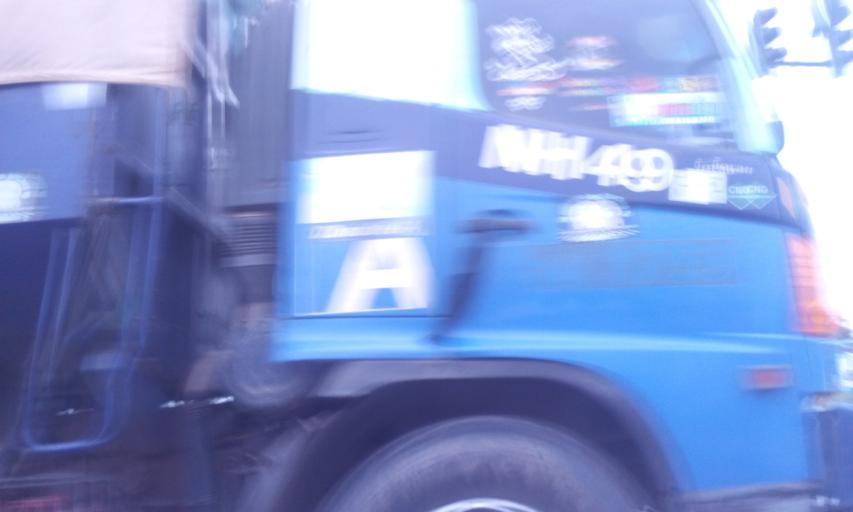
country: TH
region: Chon Buri
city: Ko Chan
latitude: 13.3247
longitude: 101.2701
